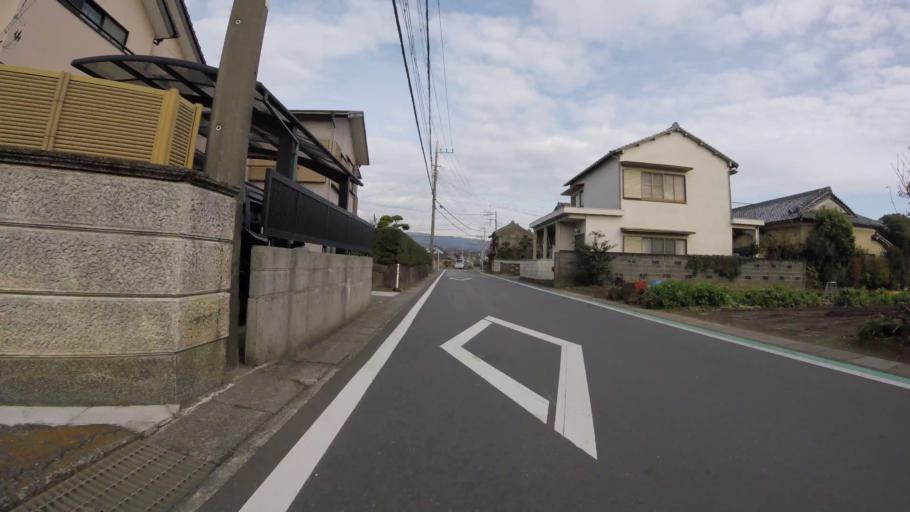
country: JP
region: Shizuoka
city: Mishima
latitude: 35.1011
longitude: 138.9262
